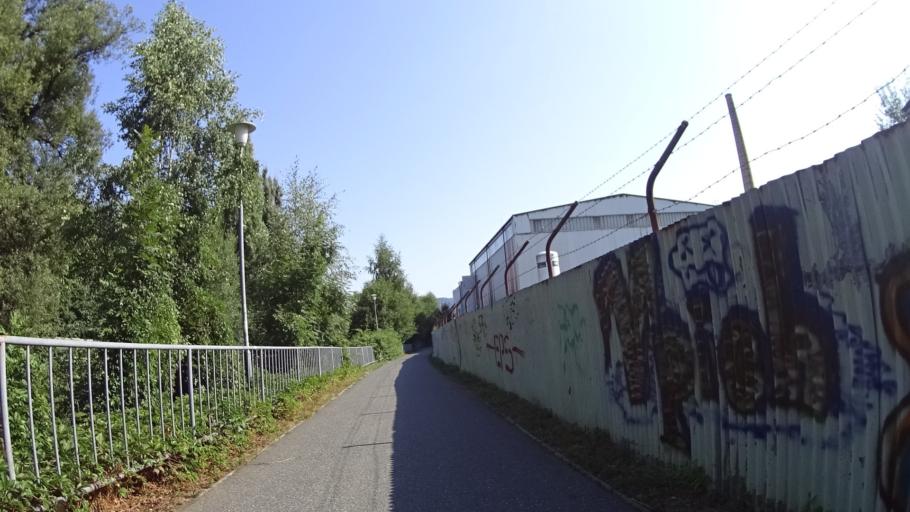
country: CZ
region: Liberecky
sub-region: Okres Liberec
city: Liberec
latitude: 50.7729
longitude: 15.0434
